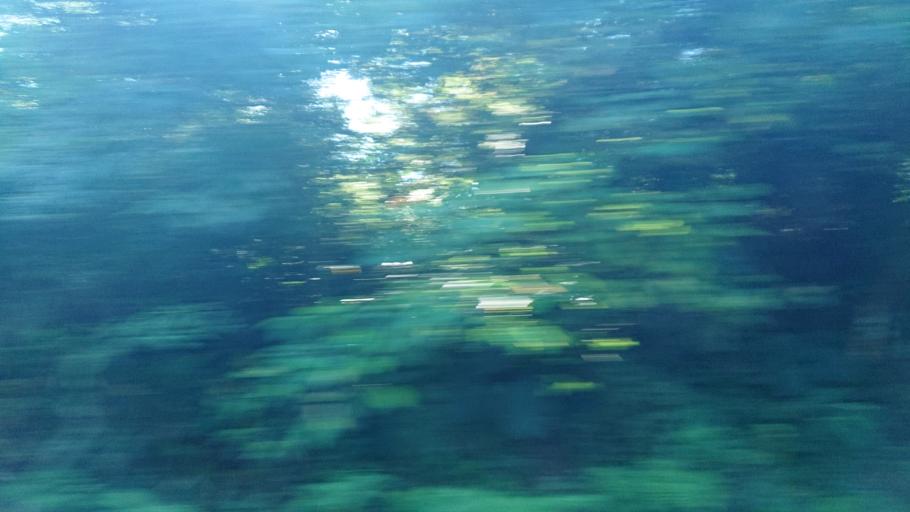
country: TW
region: Taiwan
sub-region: Chiayi
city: Jiayi Shi
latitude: 23.5357
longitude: 120.6292
